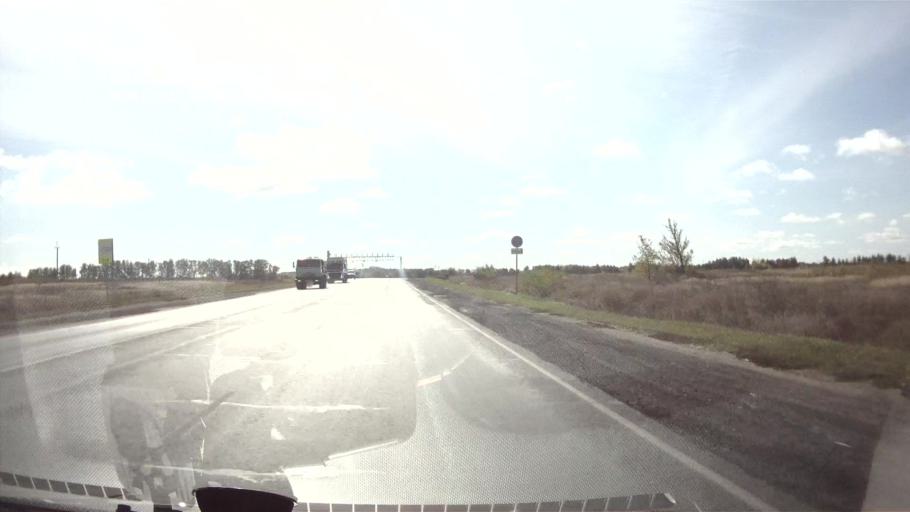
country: RU
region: Ulyanovsk
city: Isheyevka
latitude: 54.3000
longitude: 48.2454
